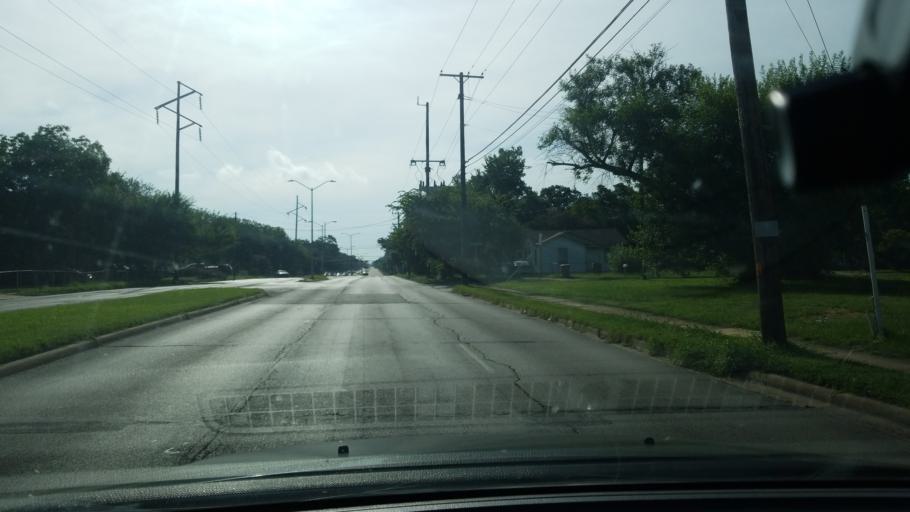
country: US
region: Texas
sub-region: Dallas County
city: Balch Springs
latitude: 32.7195
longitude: -96.6600
